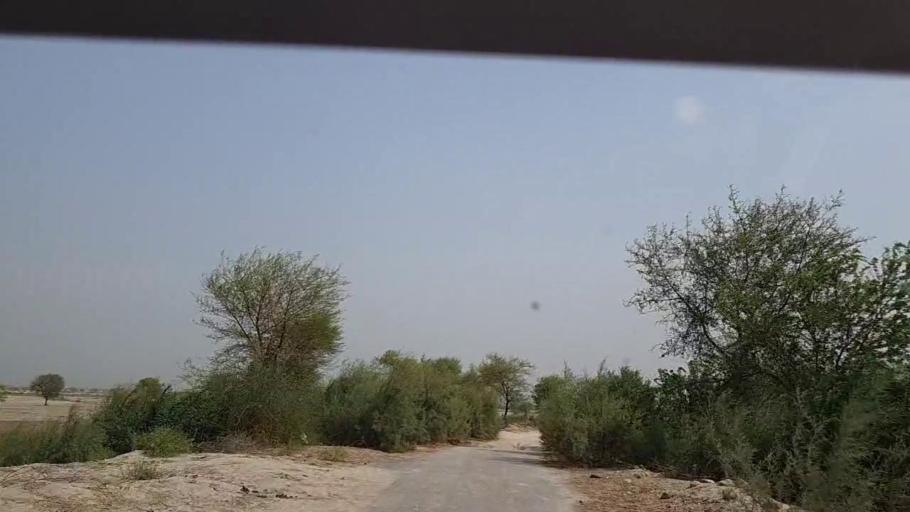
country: PK
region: Sindh
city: Khairpur Nathan Shah
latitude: 27.0288
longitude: 67.6752
